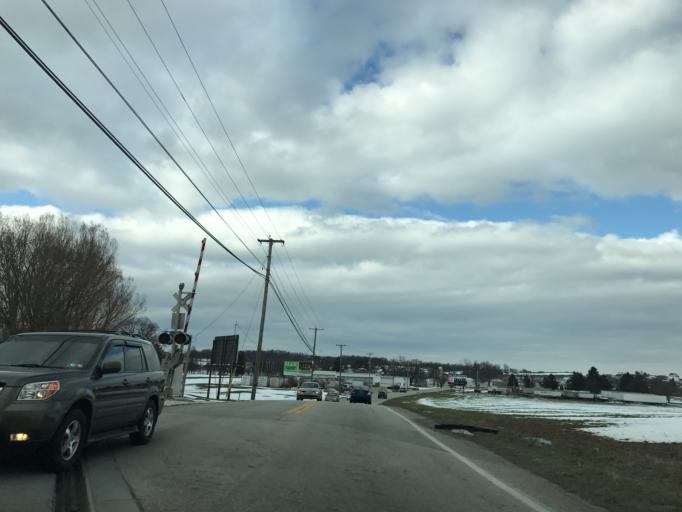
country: US
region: Pennsylvania
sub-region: York County
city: Spring Grove
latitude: 39.8929
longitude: -76.8576
